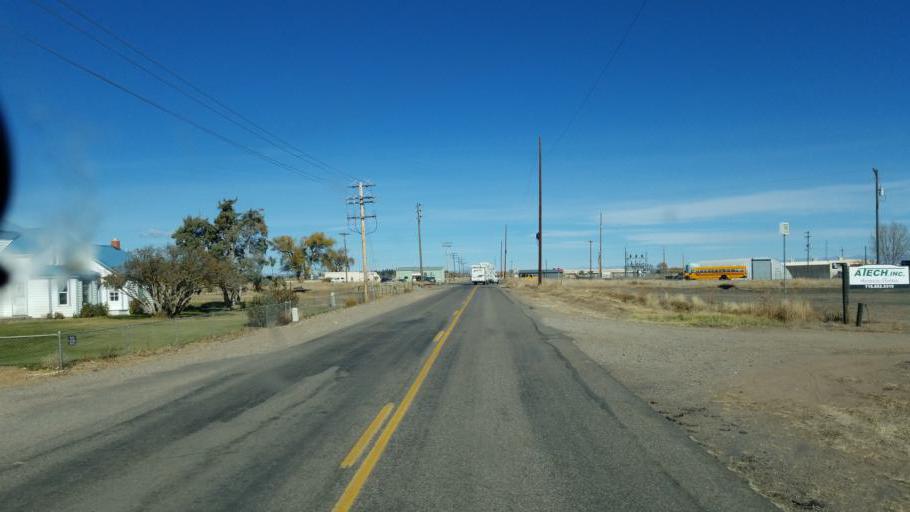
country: US
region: Colorado
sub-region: Rio Grande County
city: Monte Vista
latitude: 37.5582
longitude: -106.0941
